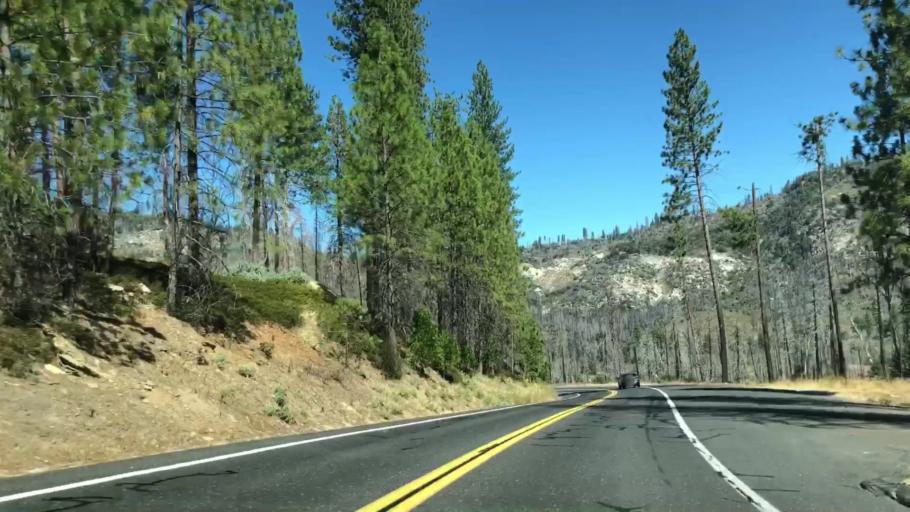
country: US
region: California
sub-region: Mariposa County
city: Midpines
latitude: 37.8160
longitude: -119.9102
